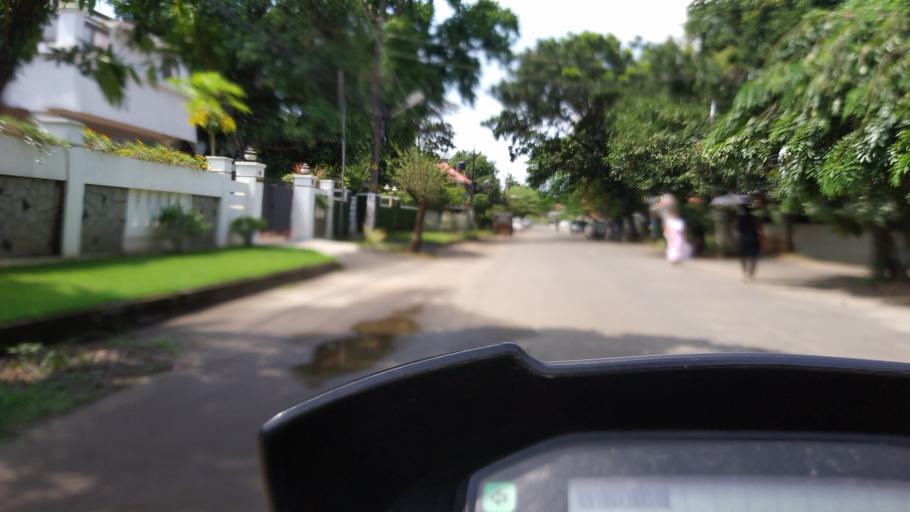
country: IN
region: Kerala
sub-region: Ernakulam
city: Cochin
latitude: 9.9735
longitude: 76.3007
